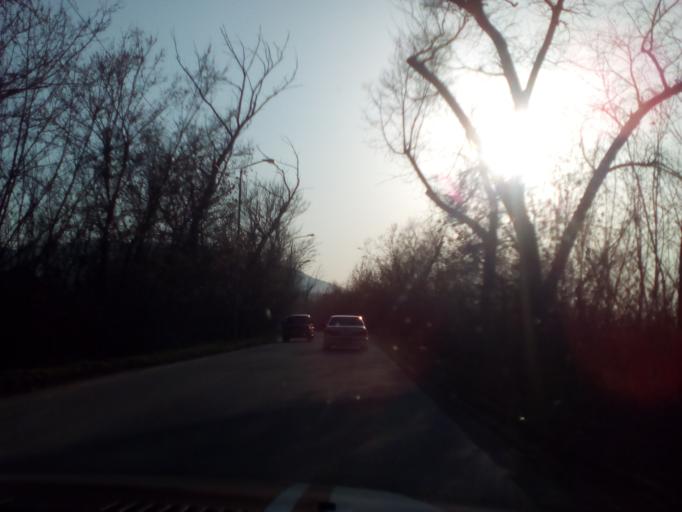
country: KZ
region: Almaty Oblysy
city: Burunday
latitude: 43.1623
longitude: 76.4586
